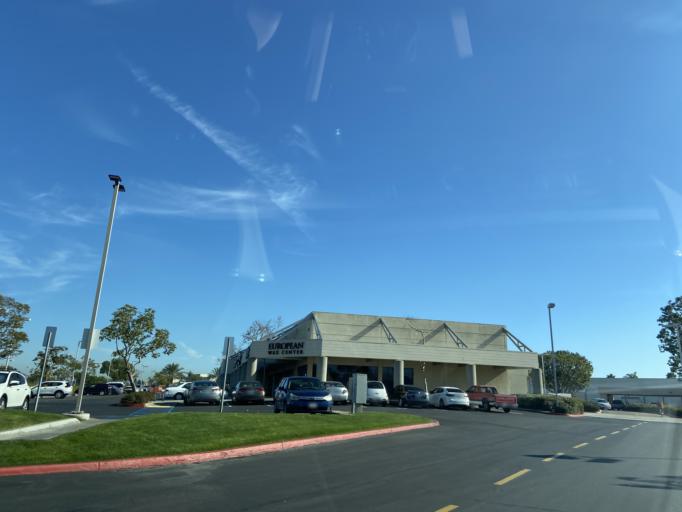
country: US
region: California
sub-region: San Diego County
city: La Jolla
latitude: 32.8215
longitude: -117.1822
